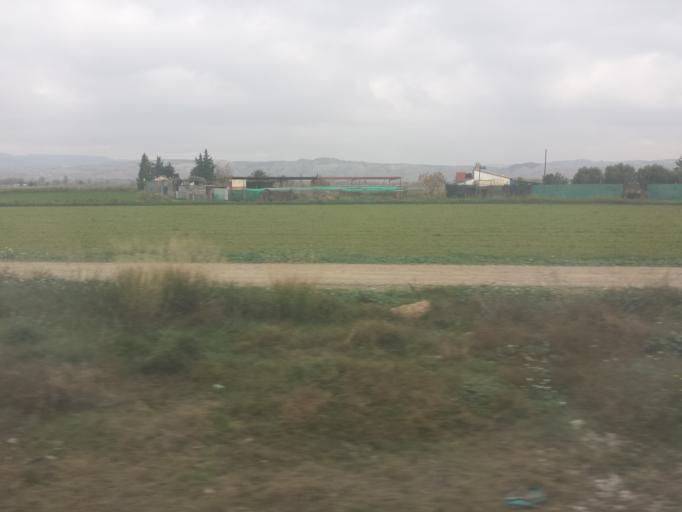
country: ES
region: Aragon
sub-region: Provincia de Zaragoza
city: Alagon
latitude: 41.7701
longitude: -1.1093
